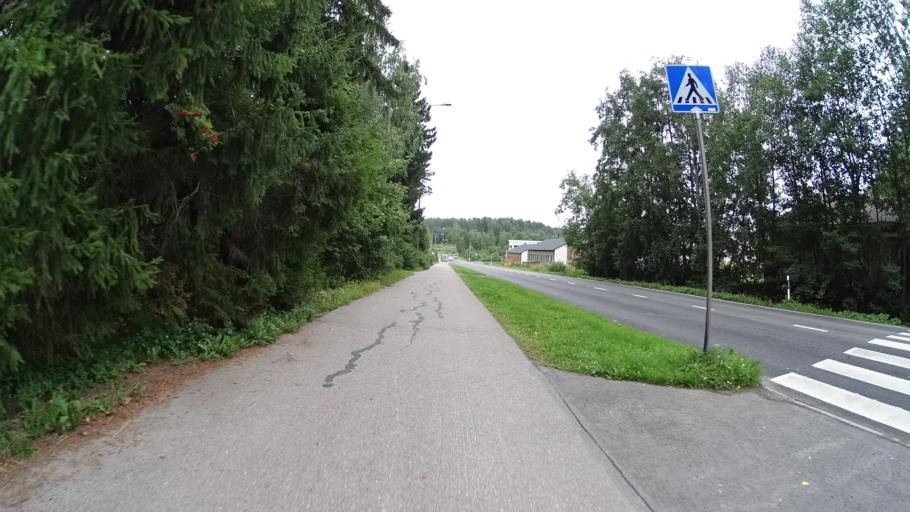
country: FI
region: Uusimaa
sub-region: Helsinki
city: Kilo
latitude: 60.2391
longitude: 24.7682
